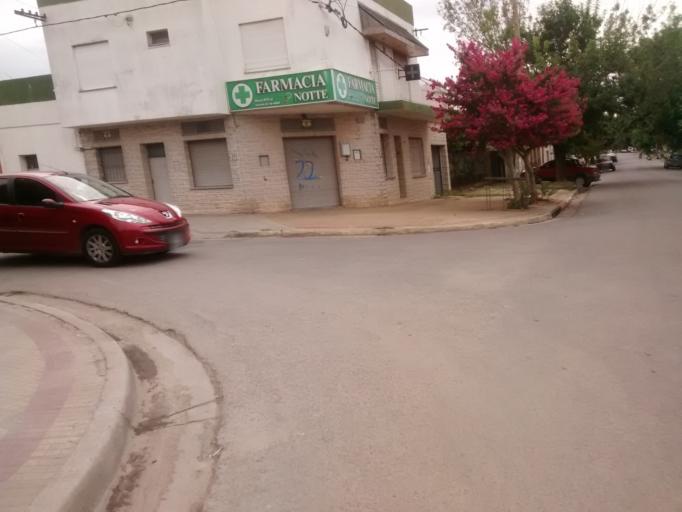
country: AR
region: Buenos Aires
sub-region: Partido de La Plata
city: La Plata
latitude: -34.9334
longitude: -57.9180
